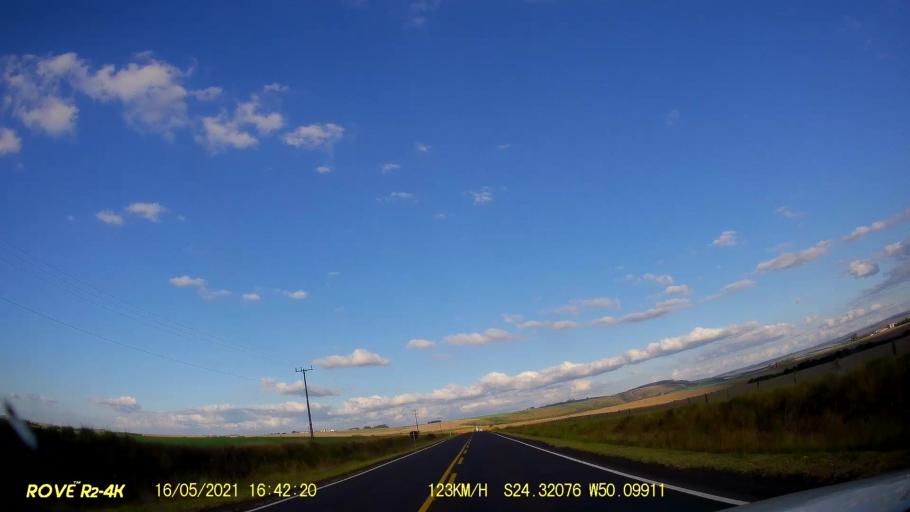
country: BR
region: Parana
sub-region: Pirai Do Sul
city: Pirai do Sul
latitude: -24.3209
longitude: -50.0981
